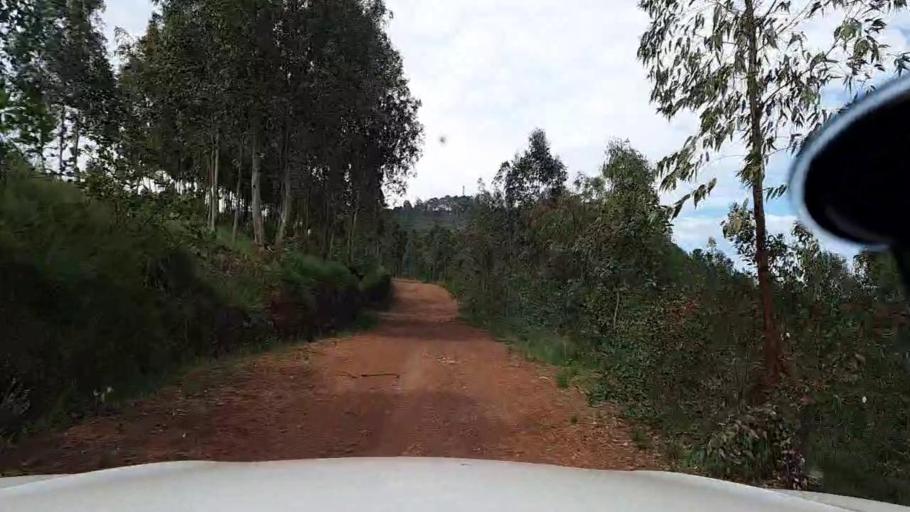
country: RW
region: Kigali
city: Kigali
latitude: -1.7907
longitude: 29.8277
